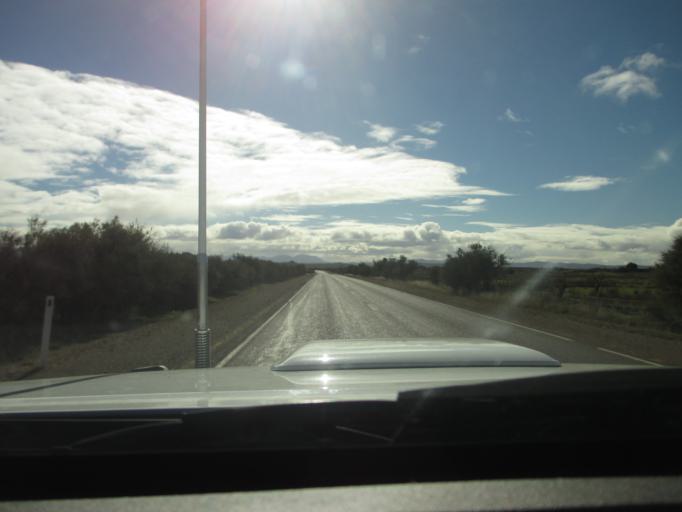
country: AU
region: South Australia
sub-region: Flinders Ranges
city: Quorn
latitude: -31.9094
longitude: 138.4332
